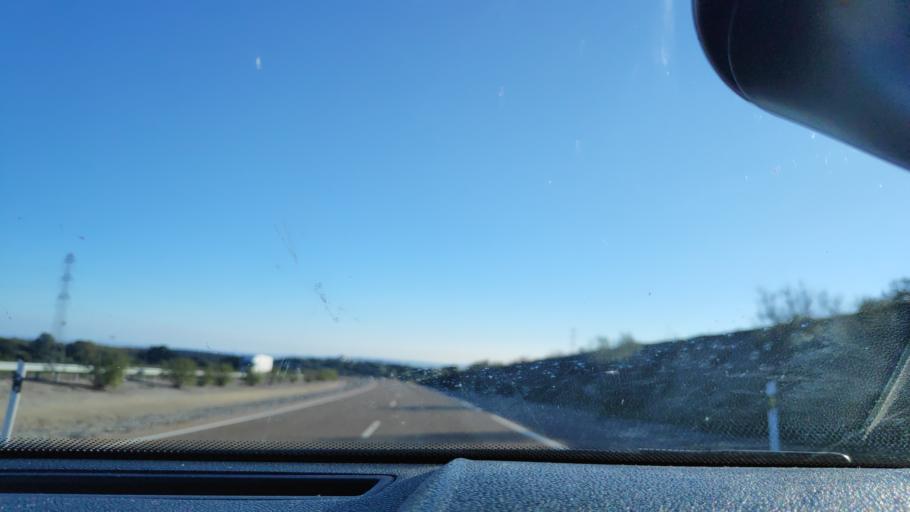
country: ES
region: Andalusia
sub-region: Provincia de Sevilla
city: Gerena
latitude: 37.5902
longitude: -6.1236
